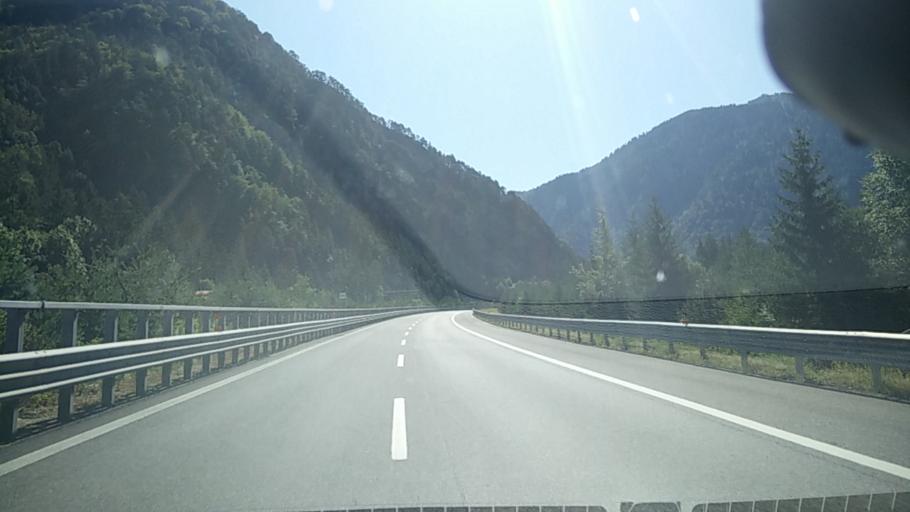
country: IT
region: Friuli Venezia Giulia
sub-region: Provincia di Udine
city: Malborghetto
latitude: 46.5063
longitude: 13.4896
